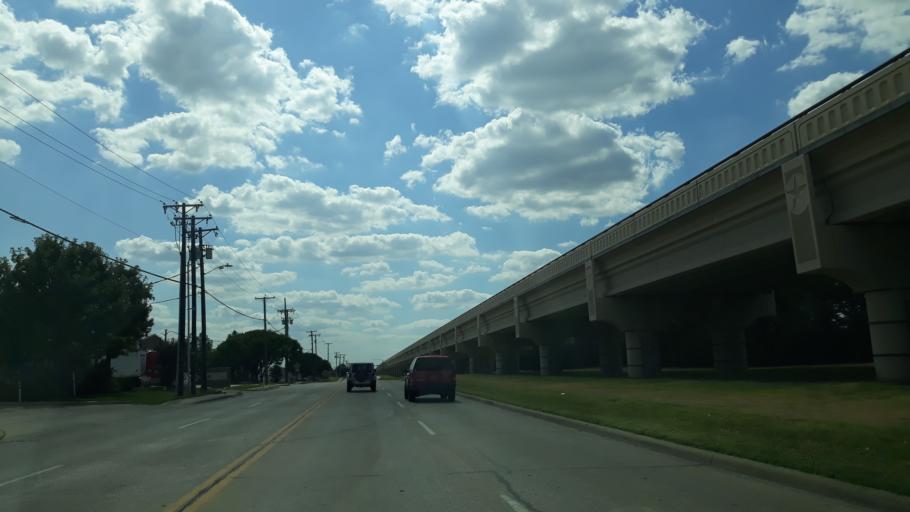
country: US
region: Texas
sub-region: Dallas County
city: Irving
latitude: 32.8155
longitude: -96.9849
